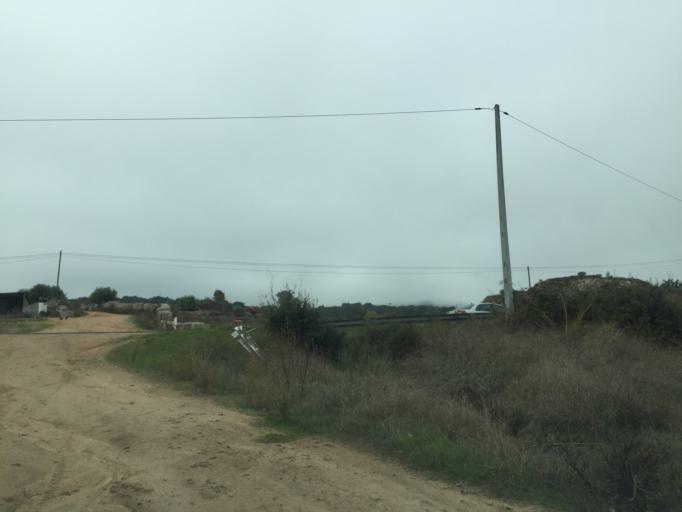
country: PT
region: Portalegre
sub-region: Arronches
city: Arronches
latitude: 39.0591
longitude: -7.4457
